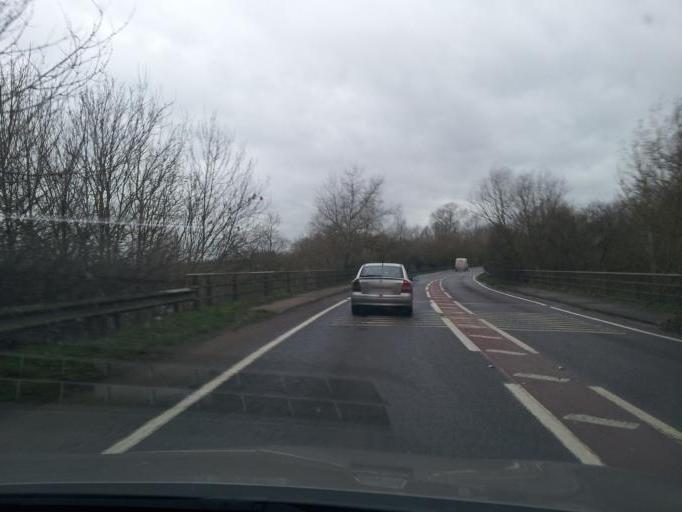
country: GB
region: England
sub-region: Suffolk
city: Ixworth
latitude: 52.2941
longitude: 0.8379
